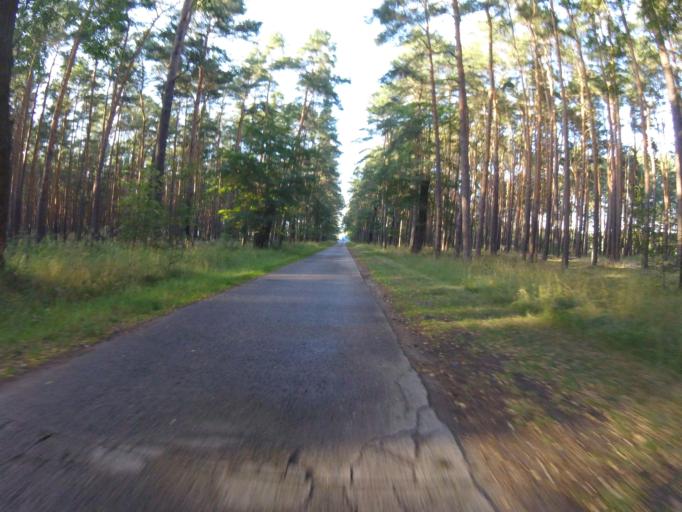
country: DE
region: Brandenburg
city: Munchehofe
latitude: 52.2136
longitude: 13.7725
